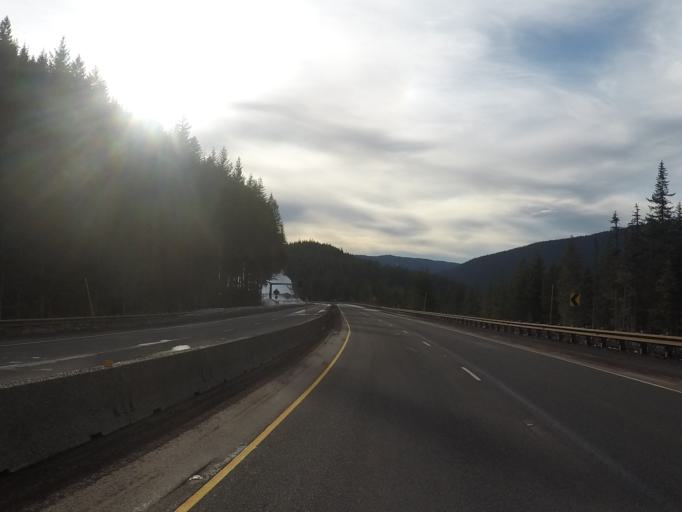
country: US
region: Oregon
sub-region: Clackamas County
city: Mount Hood Village
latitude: 45.3123
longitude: -121.7932
